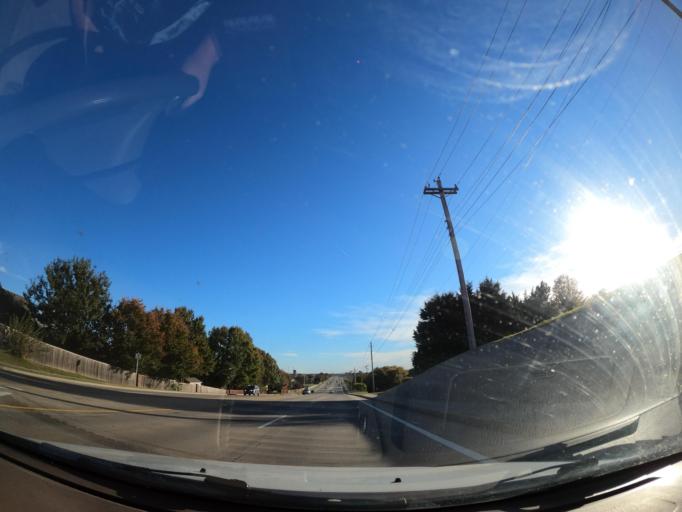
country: US
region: Oklahoma
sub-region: Tulsa County
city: Owasso
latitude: 36.2874
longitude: -95.8301
